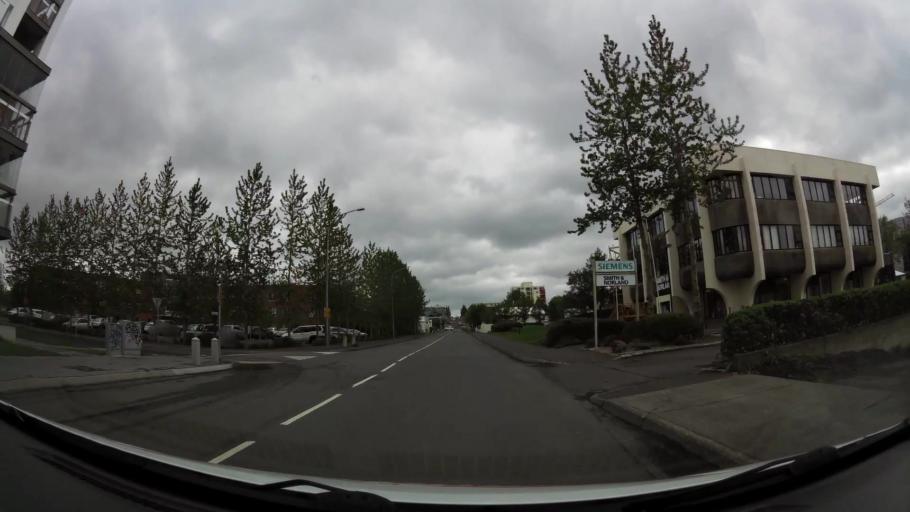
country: IS
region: Capital Region
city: Reykjavik
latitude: 64.1452
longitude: -21.9009
